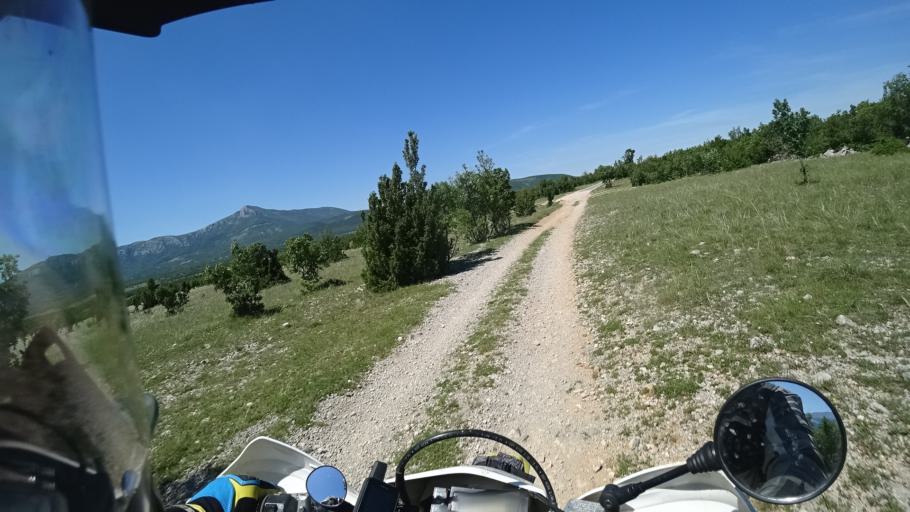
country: BA
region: Federation of Bosnia and Herzegovina
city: Bosansko Grahovo
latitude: 44.0040
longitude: 16.3843
